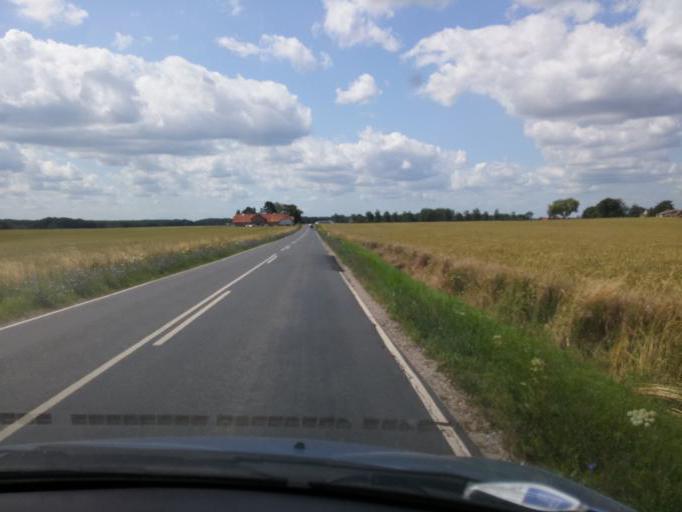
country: DK
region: South Denmark
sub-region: Kerteminde Kommune
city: Kerteminde
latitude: 55.4364
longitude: 10.6345
